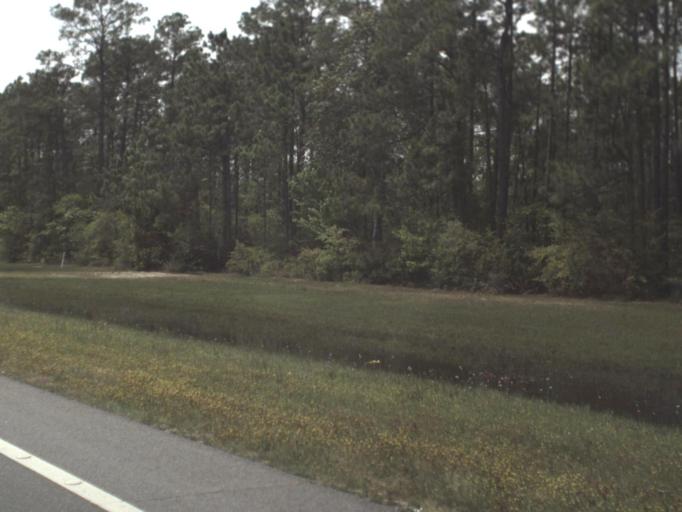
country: US
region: Florida
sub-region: Escambia County
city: Myrtle Grove
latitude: 30.4125
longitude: -87.3369
